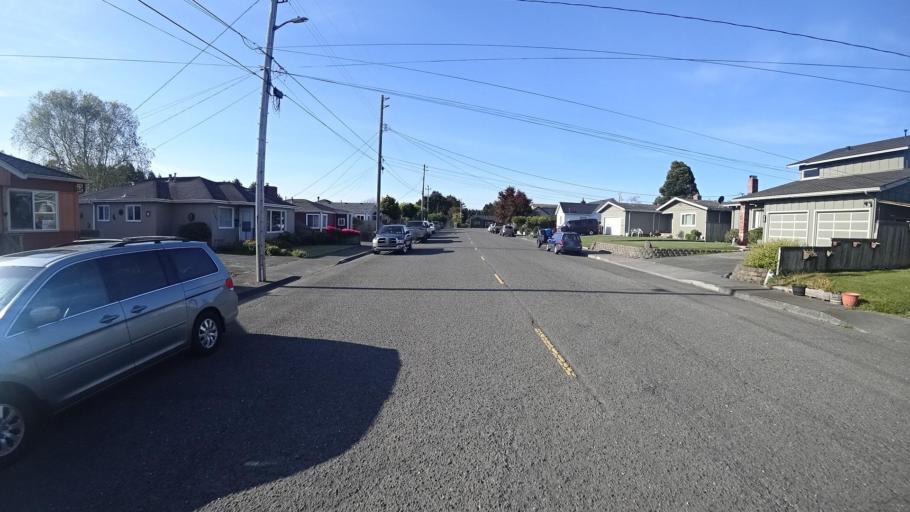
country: US
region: California
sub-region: Humboldt County
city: Bayview
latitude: 40.7669
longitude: -124.1648
